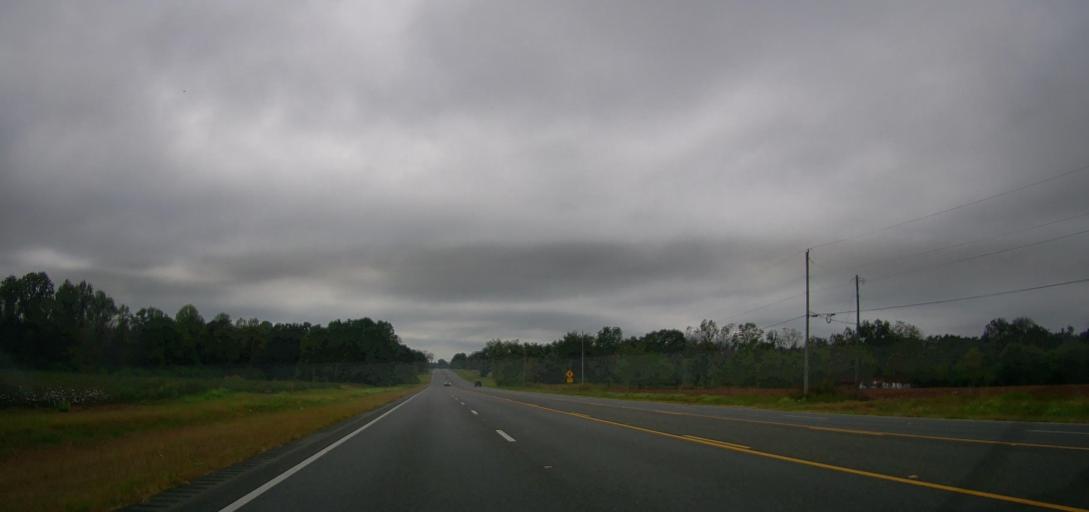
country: US
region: Georgia
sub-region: Thomas County
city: Thomasville
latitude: 30.9488
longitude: -83.8999
